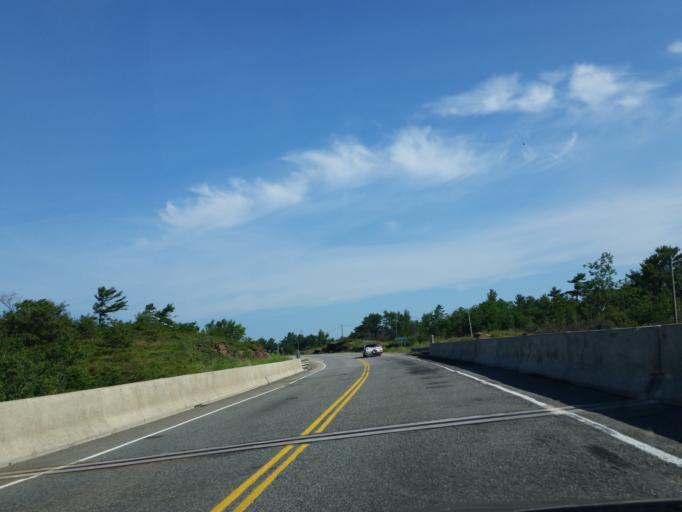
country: CA
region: Ontario
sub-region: Parry Sound District
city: Parry Sound
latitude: 45.7744
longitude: -80.4971
